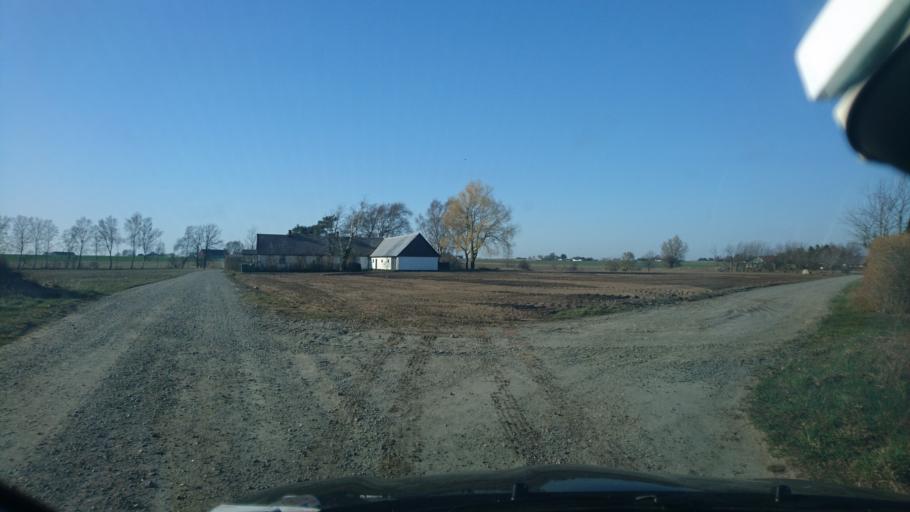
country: SE
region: Skane
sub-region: Simrishamns Kommun
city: Simrishamn
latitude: 55.4172
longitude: 14.2056
